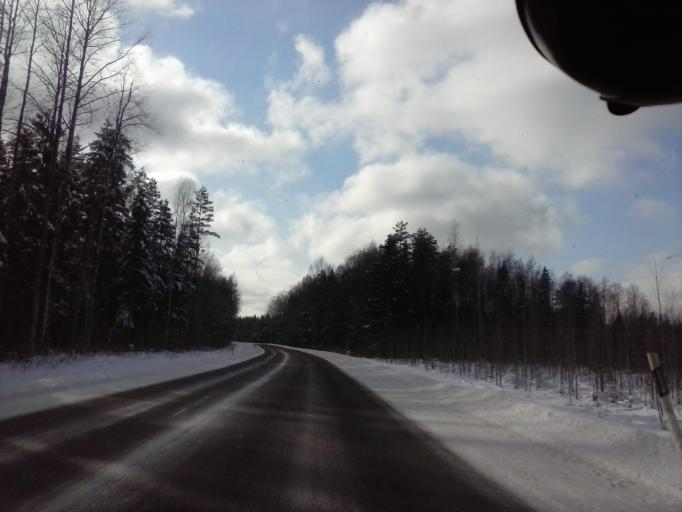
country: EE
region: Viljandimaa
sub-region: Moisakuela linn
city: Moisakula
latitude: 58.2409
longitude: 25.1268
